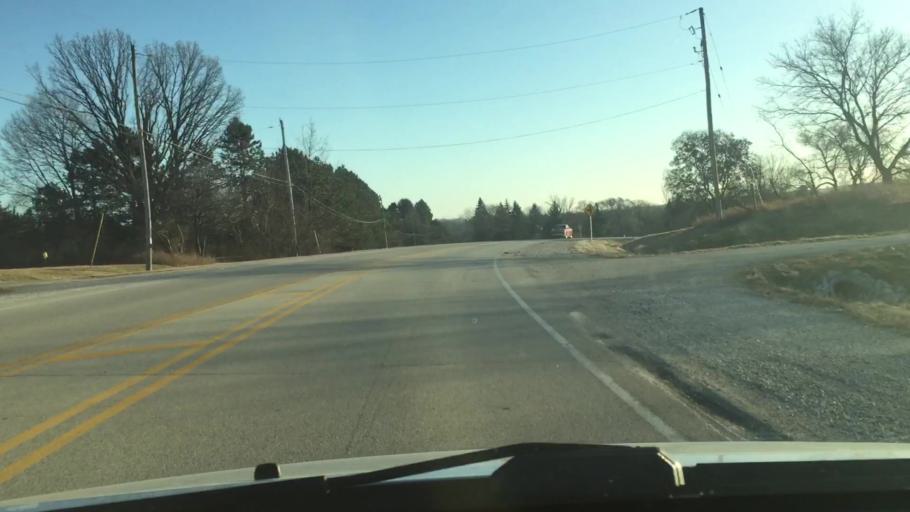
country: US
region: Wisconsin
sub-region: Waukesha County
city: Pewaukee
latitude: 43.1003
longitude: -88.2690
